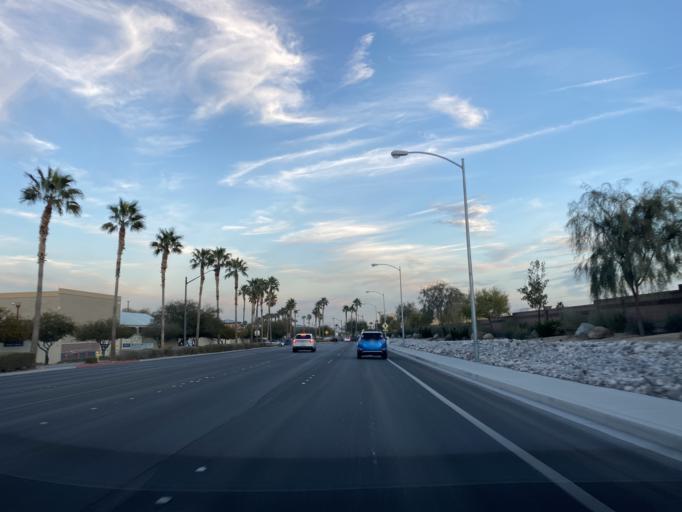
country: US
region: Nevada
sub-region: Clark County
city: Summerlin South
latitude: 36.2702
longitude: -115.2716
